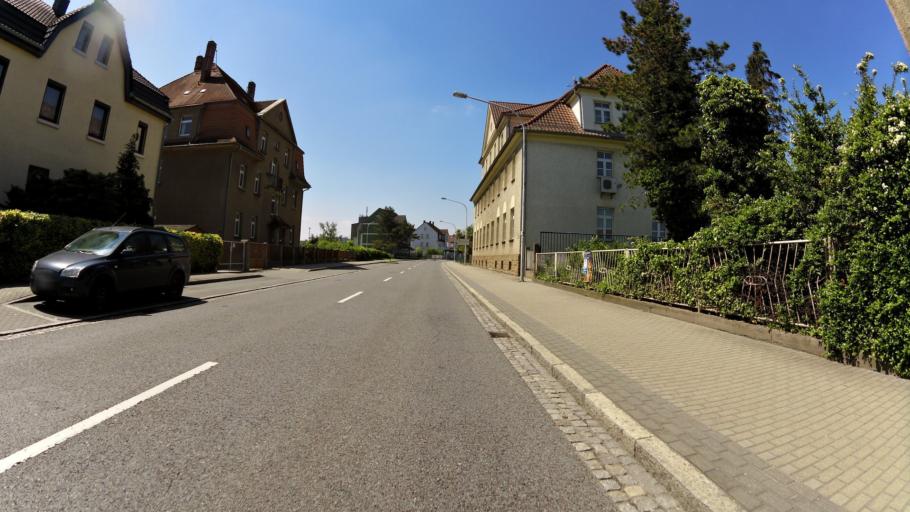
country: DE
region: Saxony
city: Riesa
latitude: 51.3175
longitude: 13.2783
